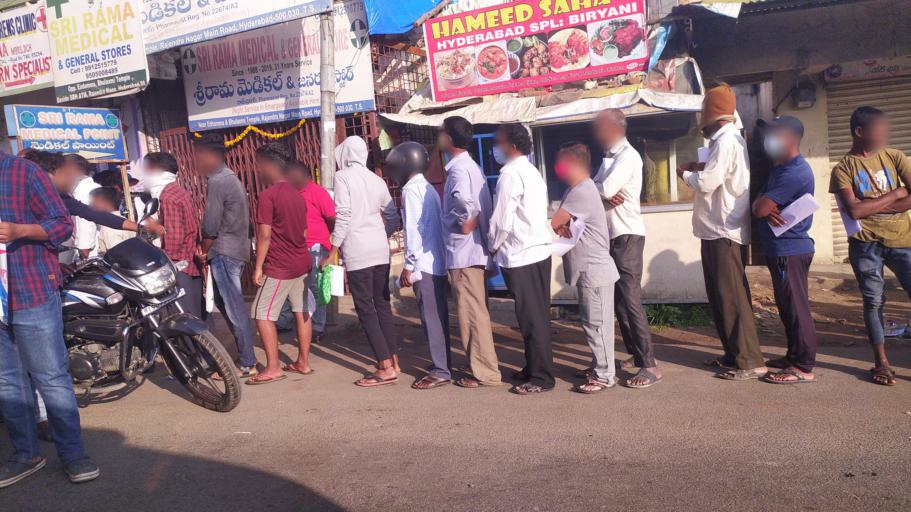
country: IN
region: Telangana
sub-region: Hyderabad
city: Hyderabad
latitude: 17.3221
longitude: 78.4026
